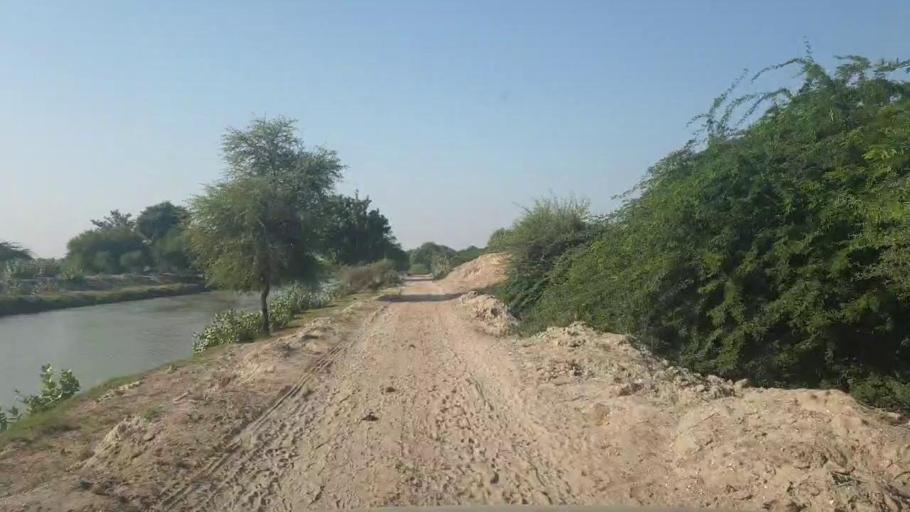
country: PK
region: Sindh
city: Tando Bago
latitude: 24.7196
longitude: 68.9166
